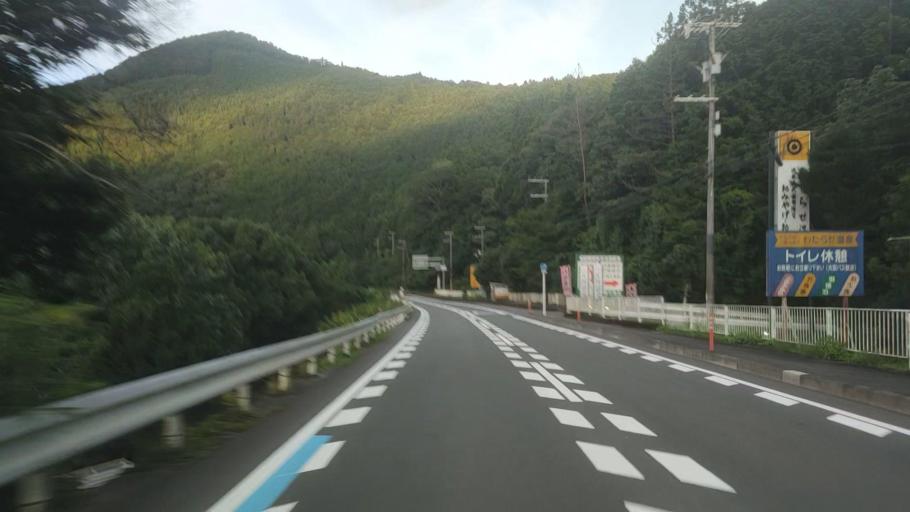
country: JP
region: Wakayama
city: Shingu
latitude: 33.8174
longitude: 135.7635
